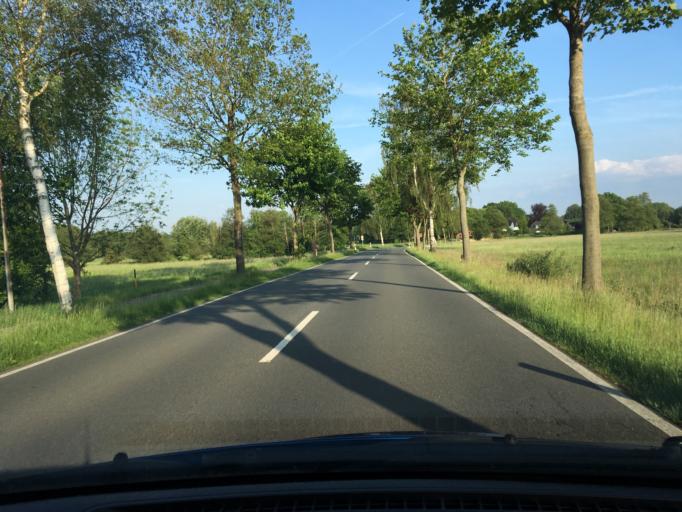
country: DE
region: Lower Saxony
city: Welle
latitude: 53.2444
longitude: 9.7956
